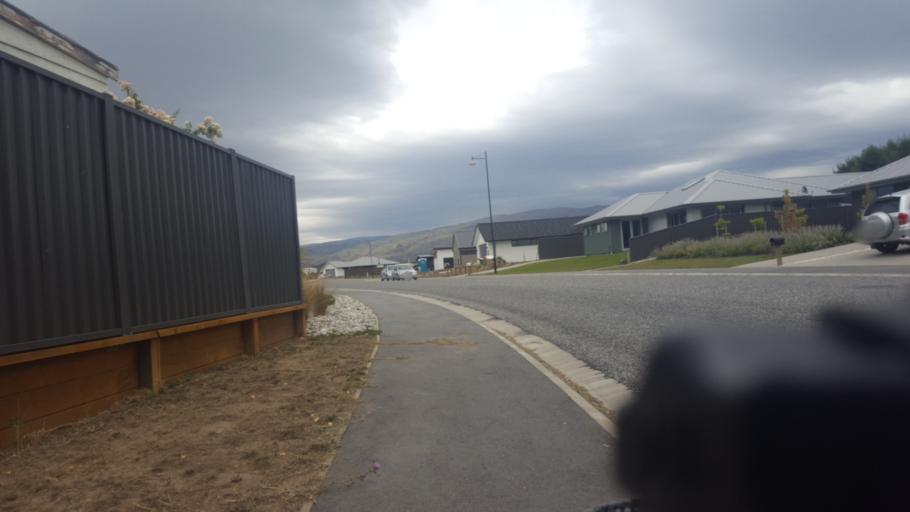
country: NZ
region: Otago
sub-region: Queenstown-Lakes District
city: Wanaka
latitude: -45.0463
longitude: 169.1829
